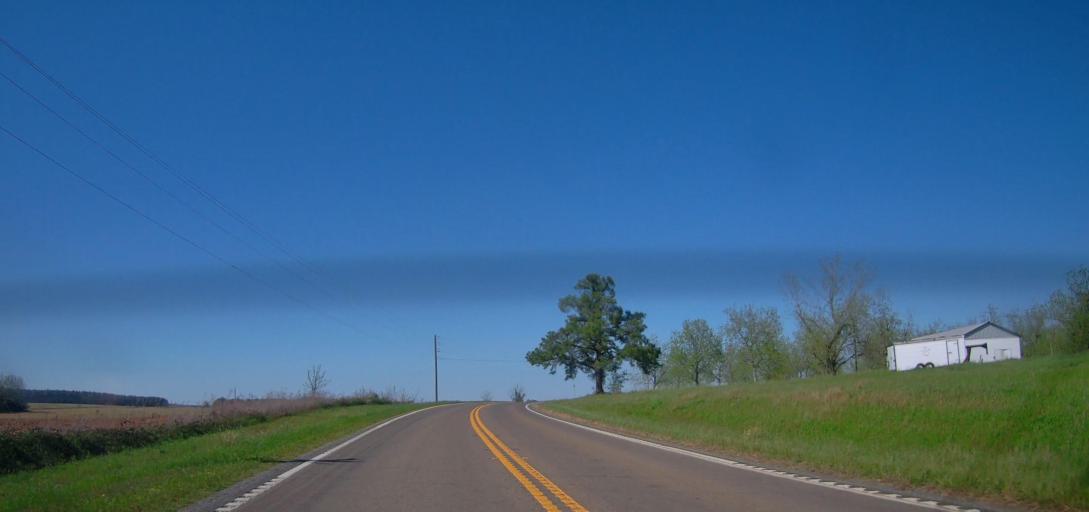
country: US
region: Georgia
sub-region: Pulaski County
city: Hawkinsville
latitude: 32.1729
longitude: -83.5104
